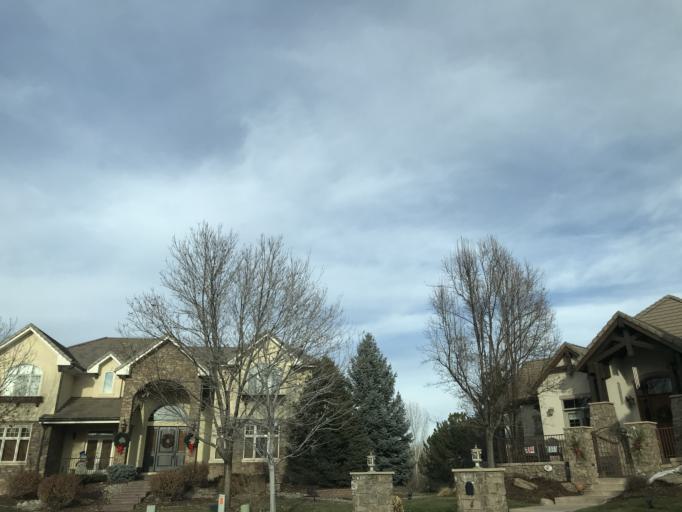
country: US
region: Colorado
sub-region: Arapahoe County
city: Columbine Valley
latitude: 39.6099
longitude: -105.0322
